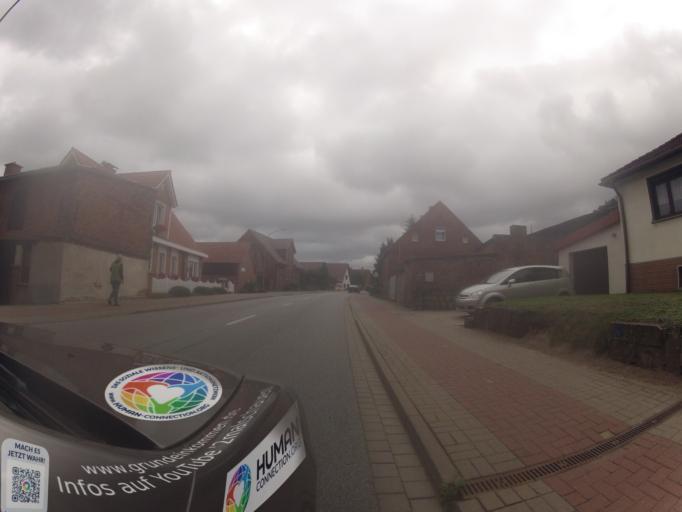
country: DE
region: Mecklenburg-Vorpommern
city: Jatznick
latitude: 53.5526
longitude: 13.9683
